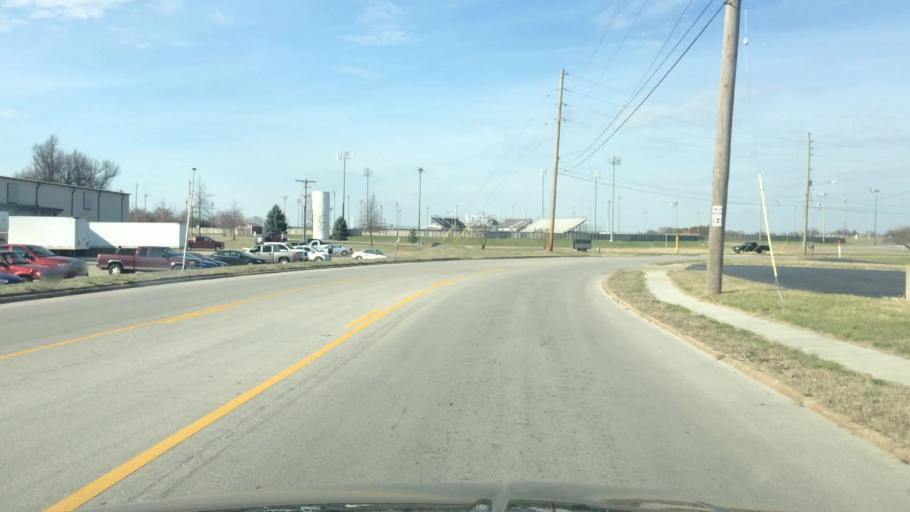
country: US
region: Missouri
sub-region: Greene County
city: Springfield
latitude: 37.2167
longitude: -93.2548
